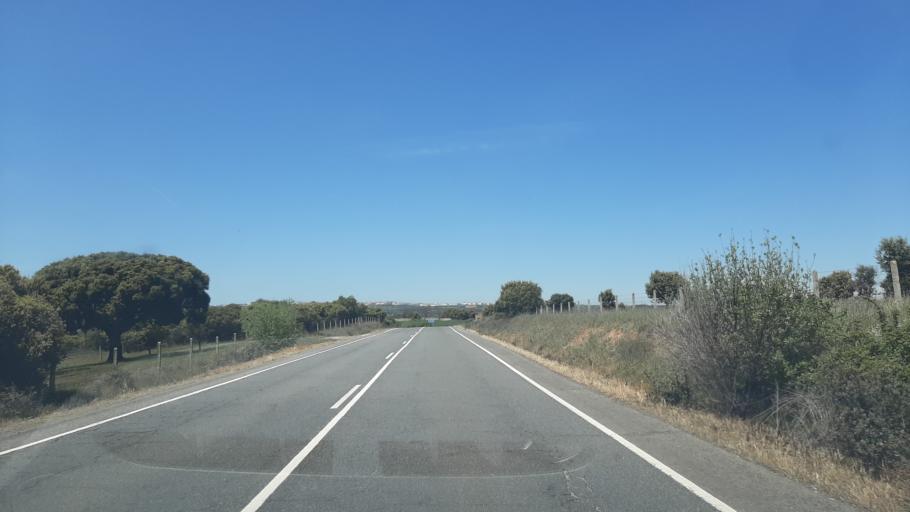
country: ES
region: Castille and Leon
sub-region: Provincia de Salamanca
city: Aldeavieja de Tormes
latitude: 40.5495
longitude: -5.6055
